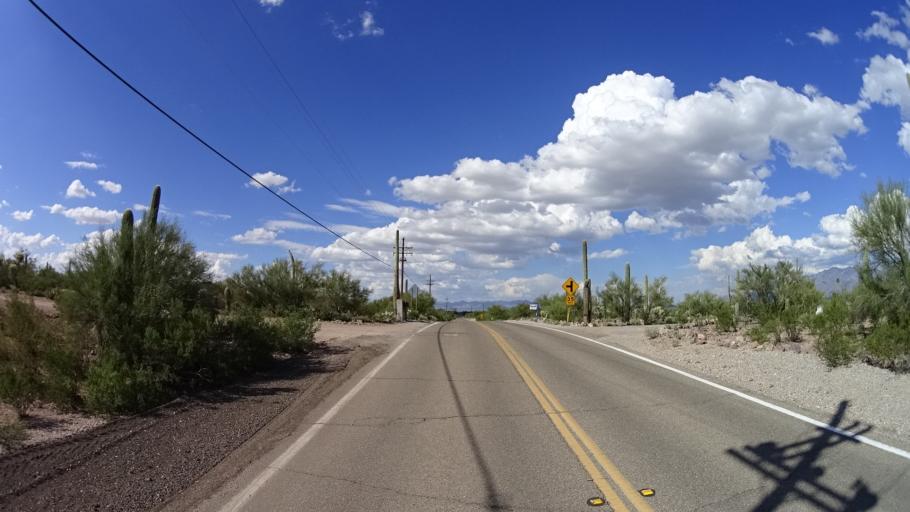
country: US
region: Arizona
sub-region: Pima County
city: Flowing Wells
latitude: 32.2634
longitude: -111.0628
